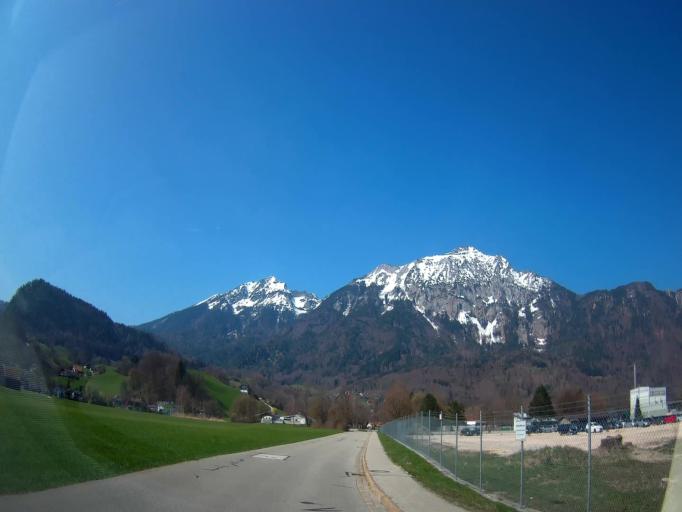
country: DE
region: Bavaria
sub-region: Upper Bavaria
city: Bad Reichenhall
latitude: 47.7229
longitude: 12.8588
